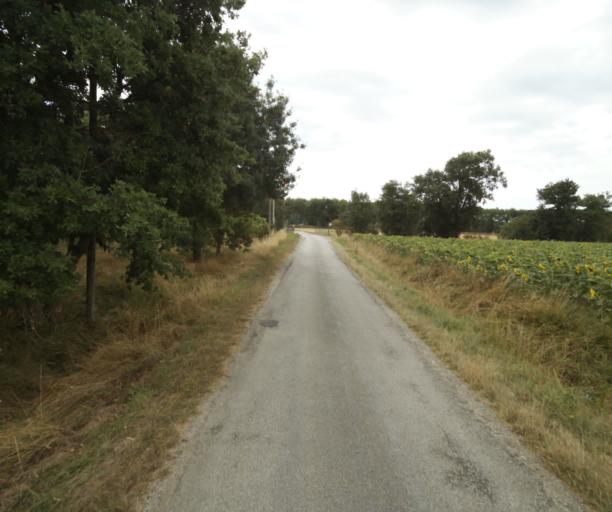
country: FR
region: Midi-Pyrenees
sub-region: Departement de la Haute-Garonne
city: Revel
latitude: 43.4314
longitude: 1.9511
